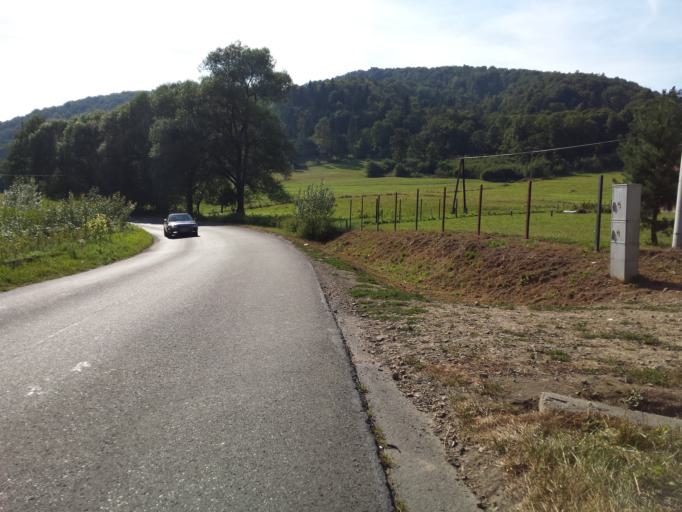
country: PL
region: Subcarpathian Voivodeship
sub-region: Powiat leski
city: Olszanica
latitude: 49.5079
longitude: 22.4598
